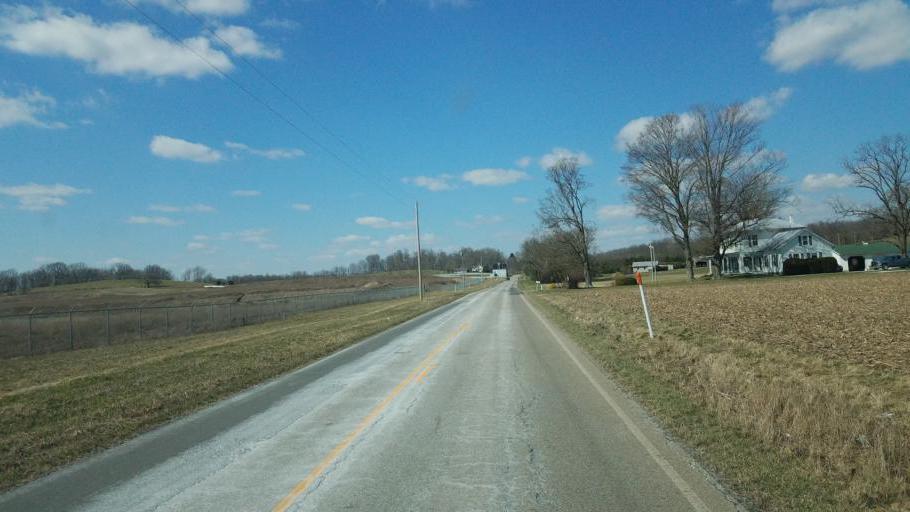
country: US
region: Ohio
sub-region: Knox County
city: Fredericktown
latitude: 40.4551
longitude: -82.5169
